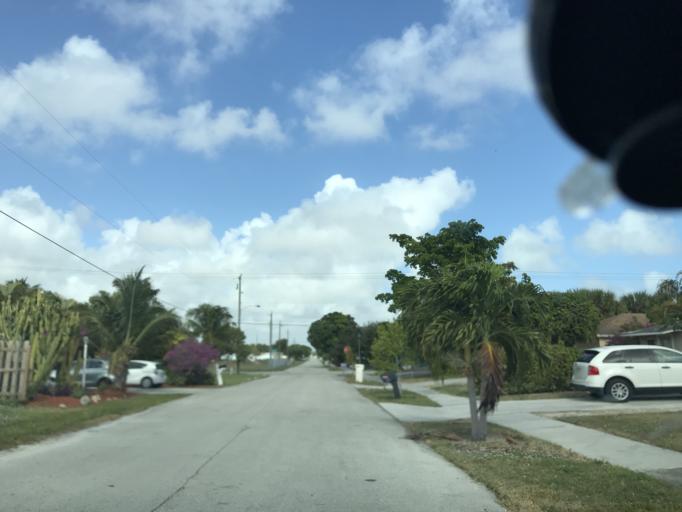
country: US
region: Florida
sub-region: Palm Beach County
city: Delray Beach
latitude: 26.4554
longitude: -80.0801
